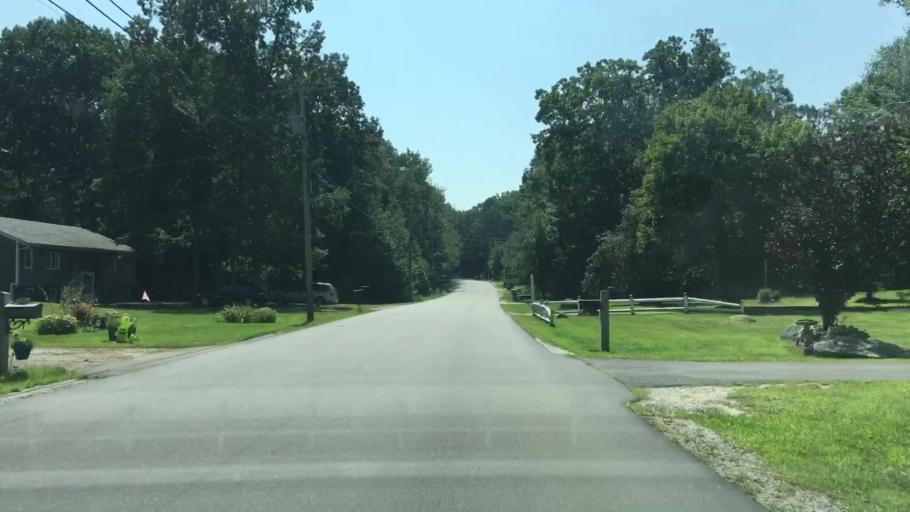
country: US
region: New Hampshire
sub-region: Rockingham County
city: Hampstead
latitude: 42.8911
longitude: -71.2175
